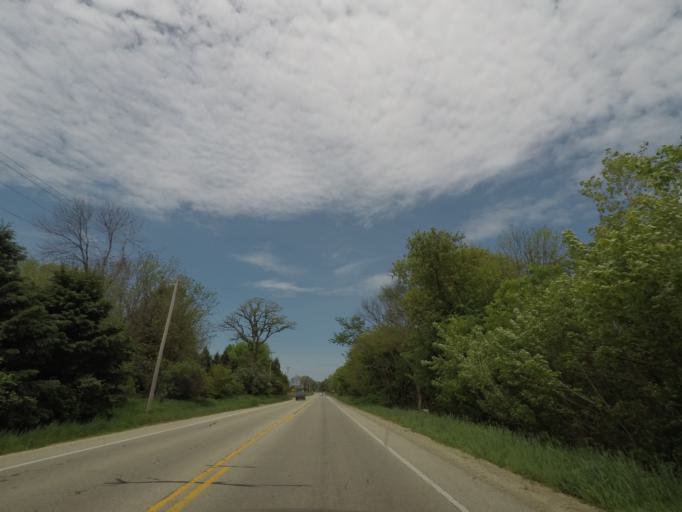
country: US
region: Wisconsin
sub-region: Green County
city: Brooklyn
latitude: 42.8568
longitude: -89.3438
